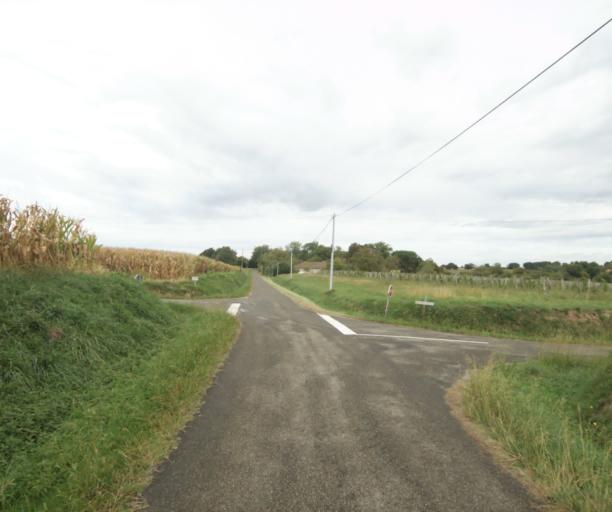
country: FR
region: Midi-Pyrenees
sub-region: Departement du Gers
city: Cazaubon
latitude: 43.8920
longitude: -0.1059
